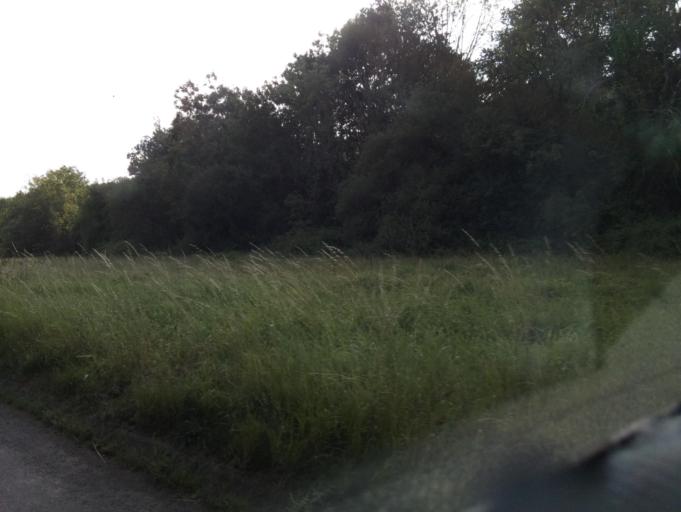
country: GB
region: England
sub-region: Devon
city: Tiverton
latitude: 50.8784
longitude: -3.4904
